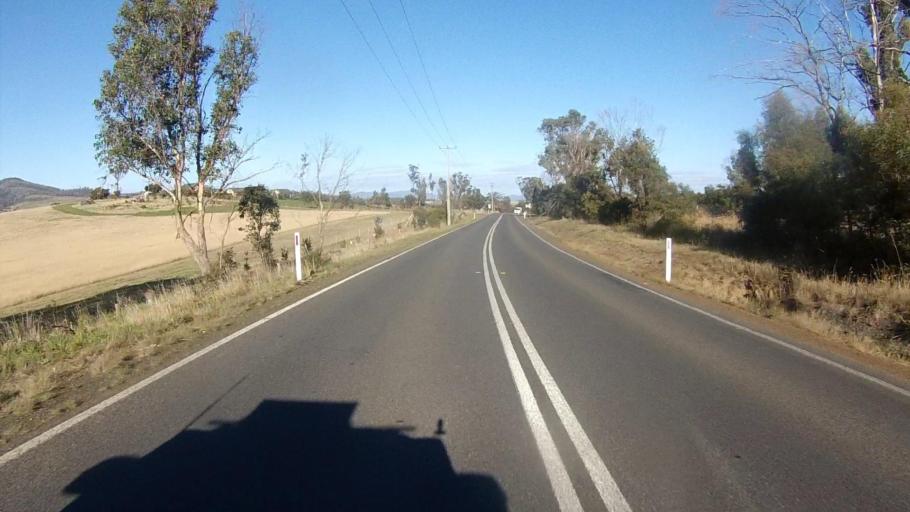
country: AU
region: Tasmania
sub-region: Sorell
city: Sorell
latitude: -42.8733
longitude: 147.8240
